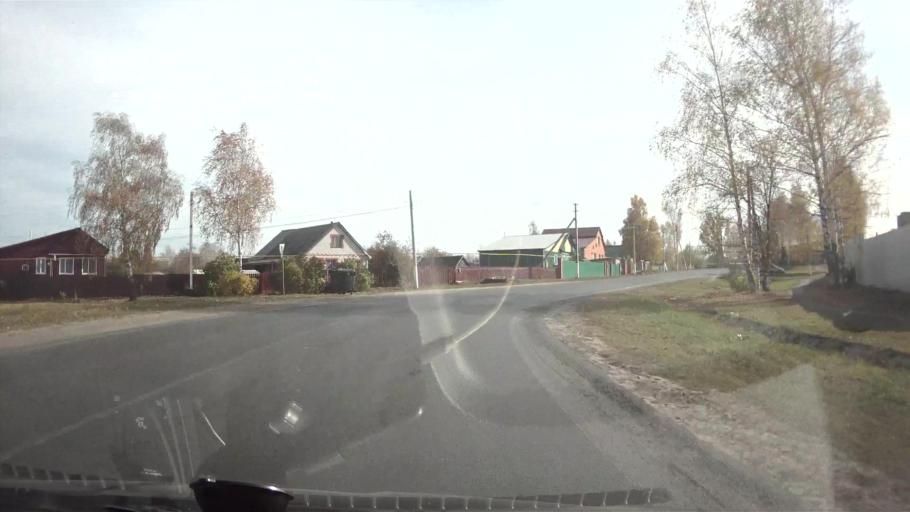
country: RU
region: Mordoviya
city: Turgenevo
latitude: 54.8451
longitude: 46.3474
